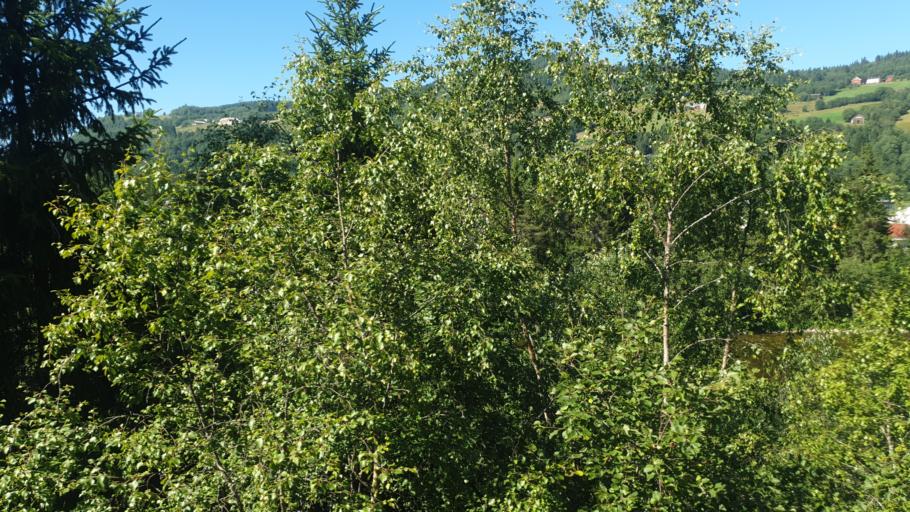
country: NO
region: Sor-Trondelag
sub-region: Meldal
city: Meldal
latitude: 63.1701
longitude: 9.7488
